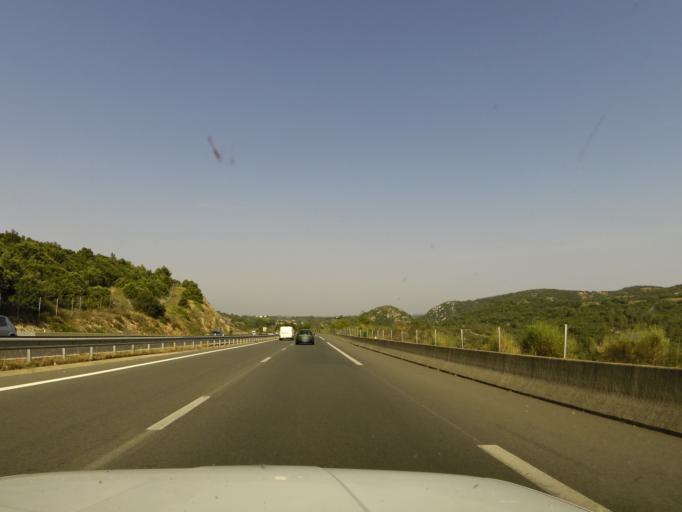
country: FR
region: Languedoc-Roussillon
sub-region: Departement de l'Herault
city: Montarnaud
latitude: 43.6256
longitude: 3.6500
